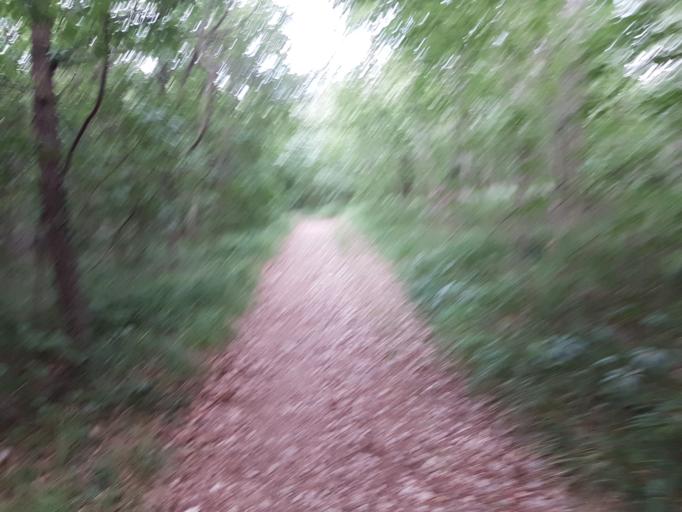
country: IT
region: Friuli Venezia Giulia
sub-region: Provincia di Trieste
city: Aurisina
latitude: 45.7485
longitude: 13.6696
